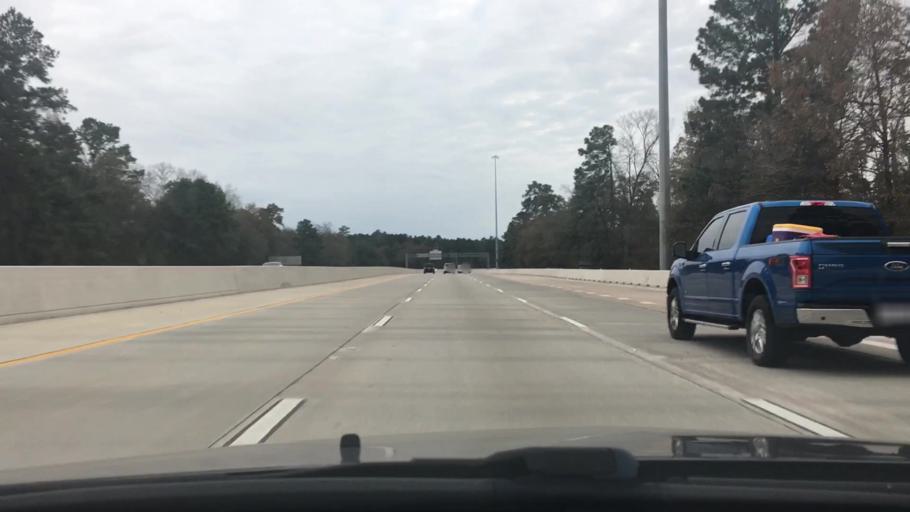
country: US
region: Texas
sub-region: Harris County
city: Spring
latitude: 30.0831
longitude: -95.4116
